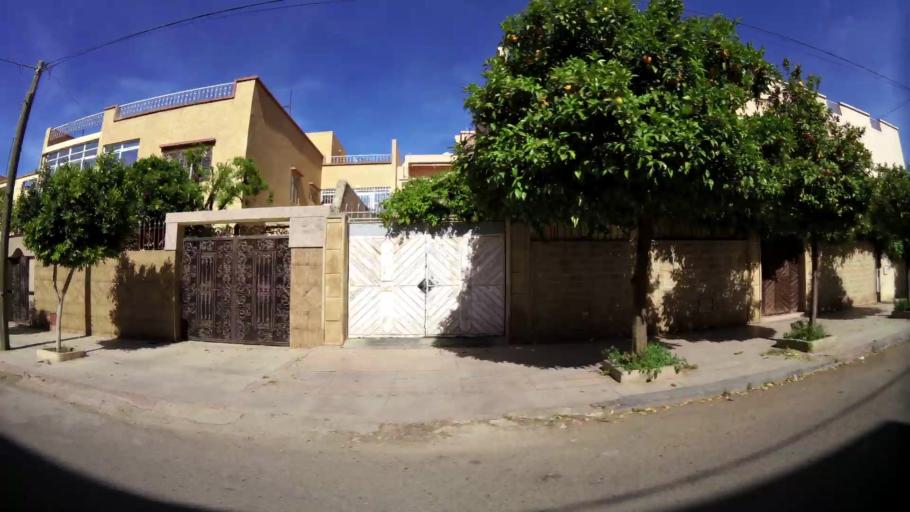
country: MA
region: Oriental
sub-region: Oujda-Angad
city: Oujda
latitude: 34.6678
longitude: -1.9105
